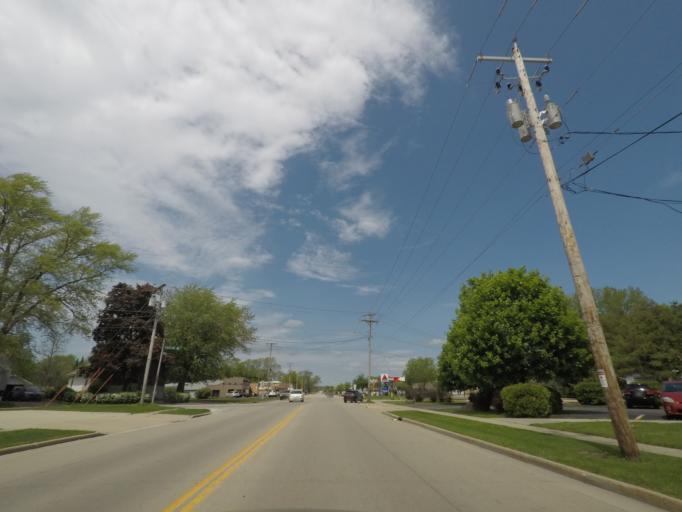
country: US
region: Wisconsin
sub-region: Rock County
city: Beloit
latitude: 42.5148
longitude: -89.0608
